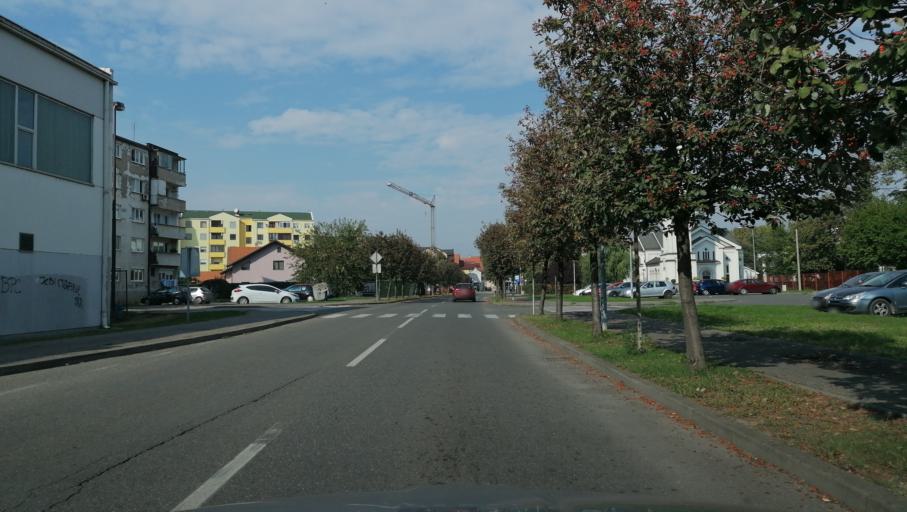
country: BA
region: Republika Srpska
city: Bijeljina
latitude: 44.7592
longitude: 19.2253
